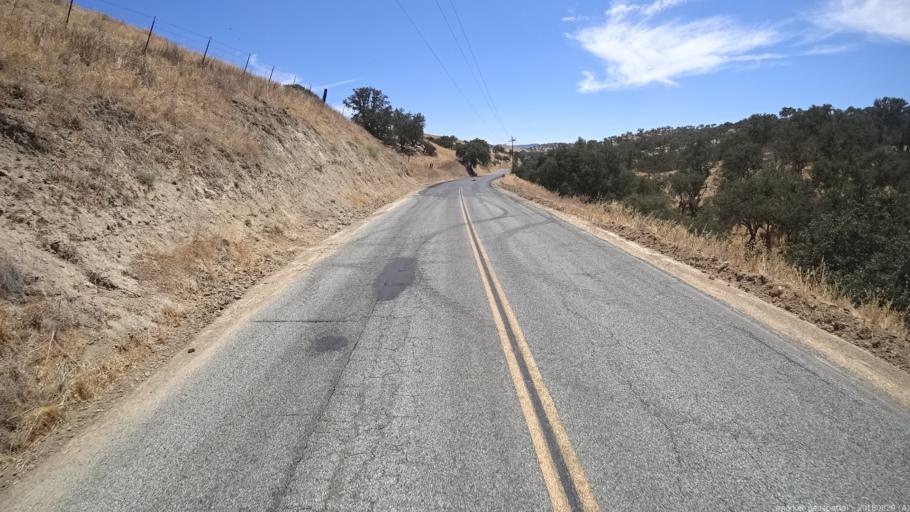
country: US
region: California
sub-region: San Luis Obispo County
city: Lake Nacimiento
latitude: 35.8244
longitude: -120.8419
